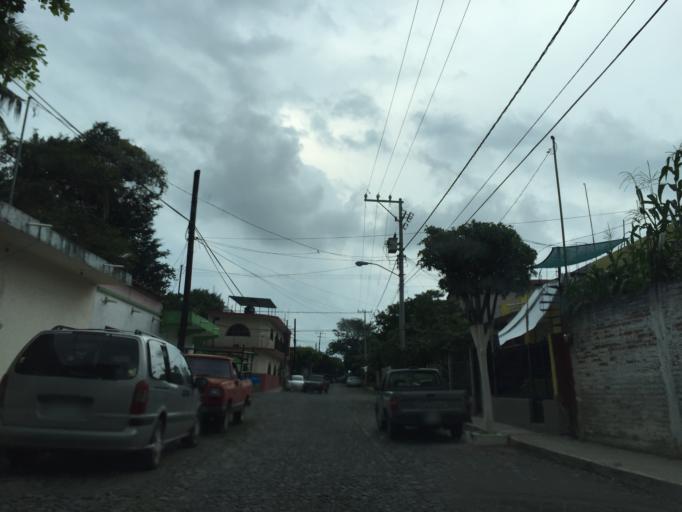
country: MX
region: Colima
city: Comala
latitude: 19.3285
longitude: -103.7591
